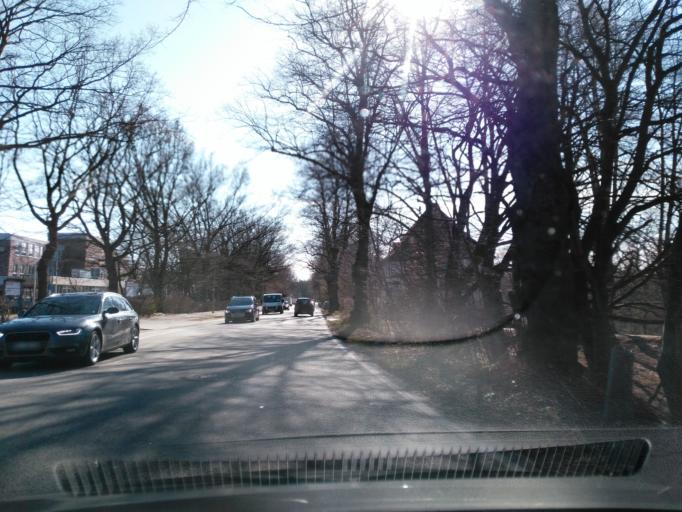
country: DE
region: Schleswig-Holstein
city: Kiel
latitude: 54.2958
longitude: 10.1036
